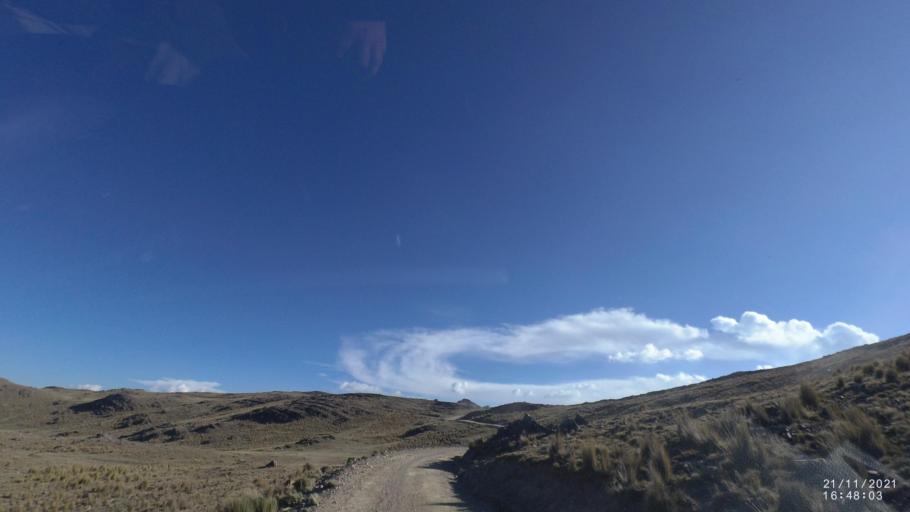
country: BO
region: Cochabamba
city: Cochabamba
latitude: -17.0787
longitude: -66.2555
